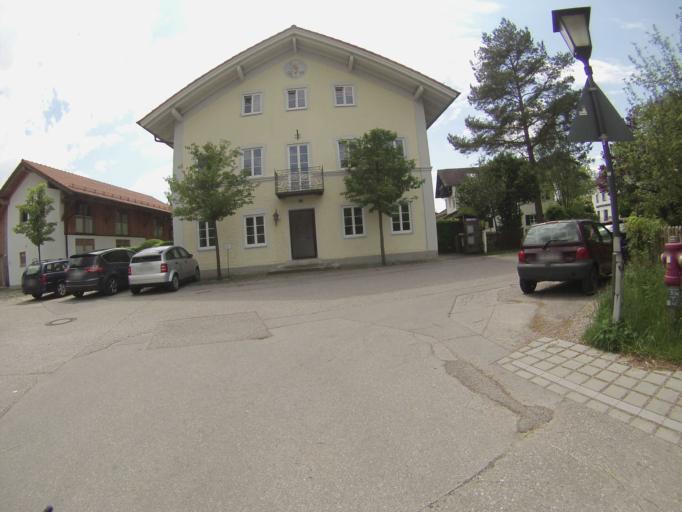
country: DE
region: Bavaria
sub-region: Upper Bavaria
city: Aying
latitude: 47.9698
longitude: 11.7788
